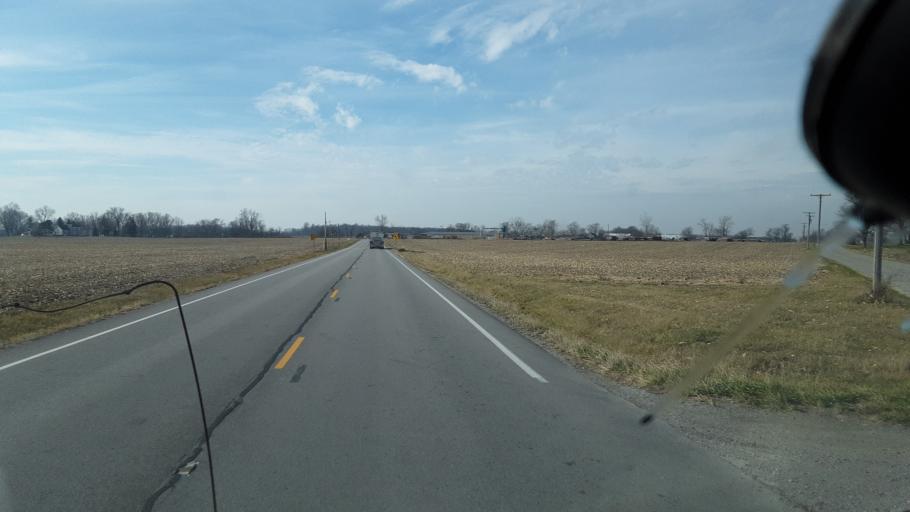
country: US
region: Indiana
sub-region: Allen County
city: Harlan
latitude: 41.2258
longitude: -84.8806
